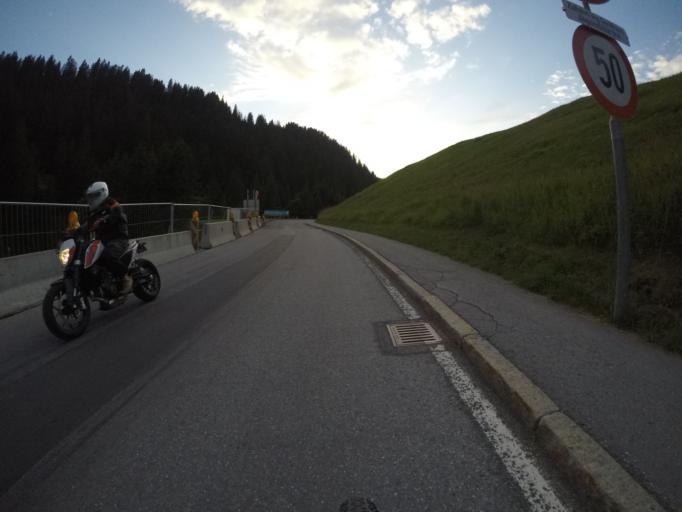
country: AT
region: Vorarlberg
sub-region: Politischer Bezirk Bregenz
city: Damuels
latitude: 47.2844
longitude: 9.8904
